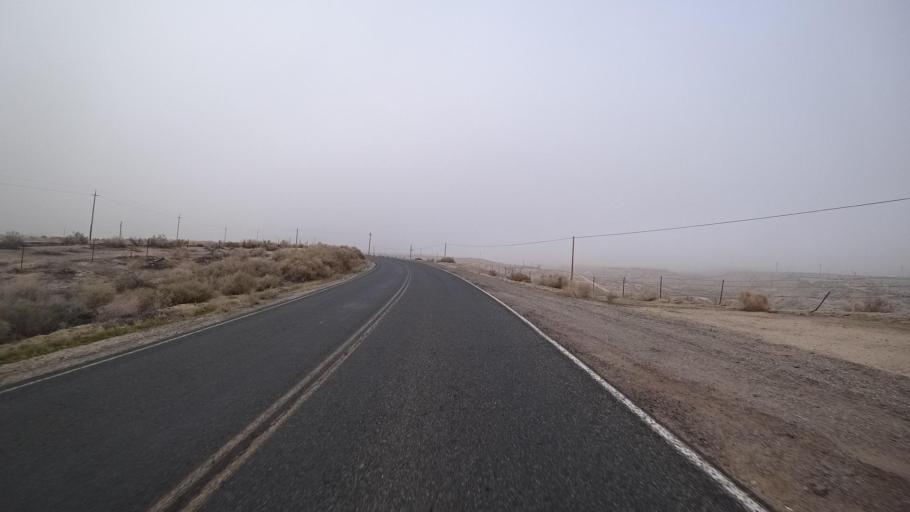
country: US
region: California
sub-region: Kern County
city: Ford City
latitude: 35.2631
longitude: -119.4631
